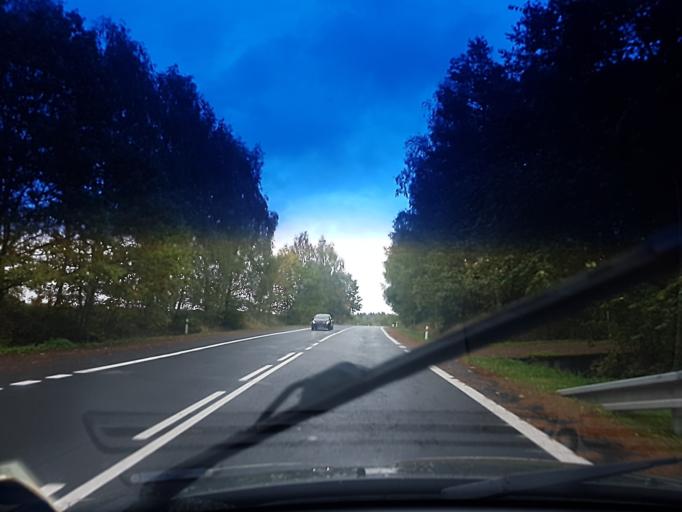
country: CZ
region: Karlovarsky
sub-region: Okres Cheb
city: Frantiskovy Lazne
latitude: 50.0846
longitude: 12.3001
